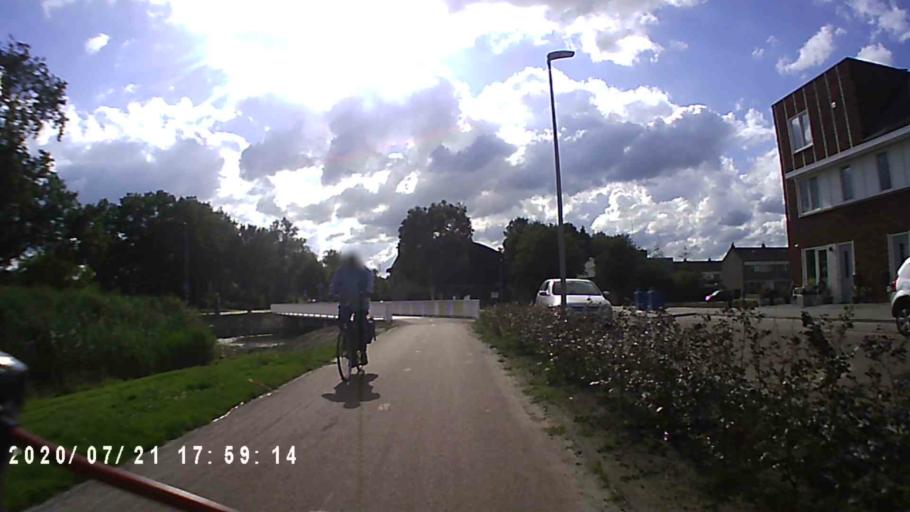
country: NL
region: Groningen
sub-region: Gemeente Hoogezand-Sappemeer
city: Hoogezand
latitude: 53.1518
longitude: 6.7500
